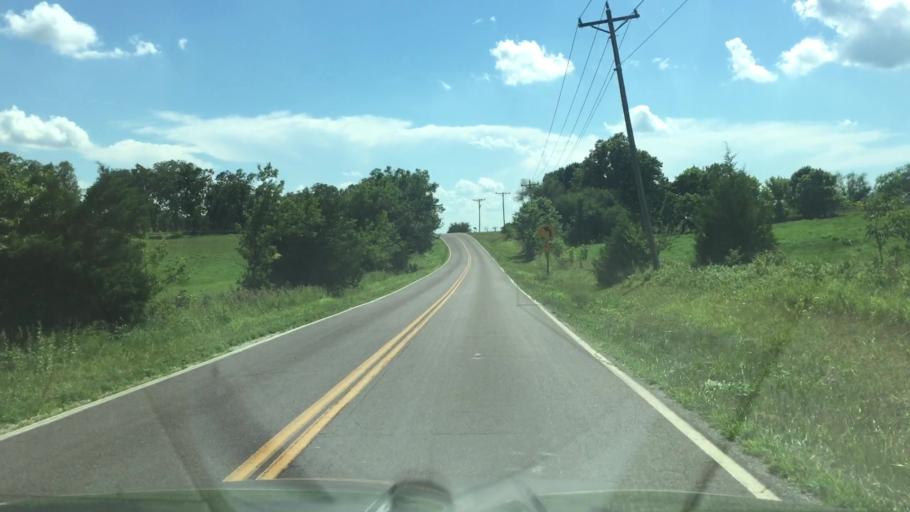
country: US
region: Missouri
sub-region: Miller County
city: Tuscumbia
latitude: 38.1252
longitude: -92.4642
